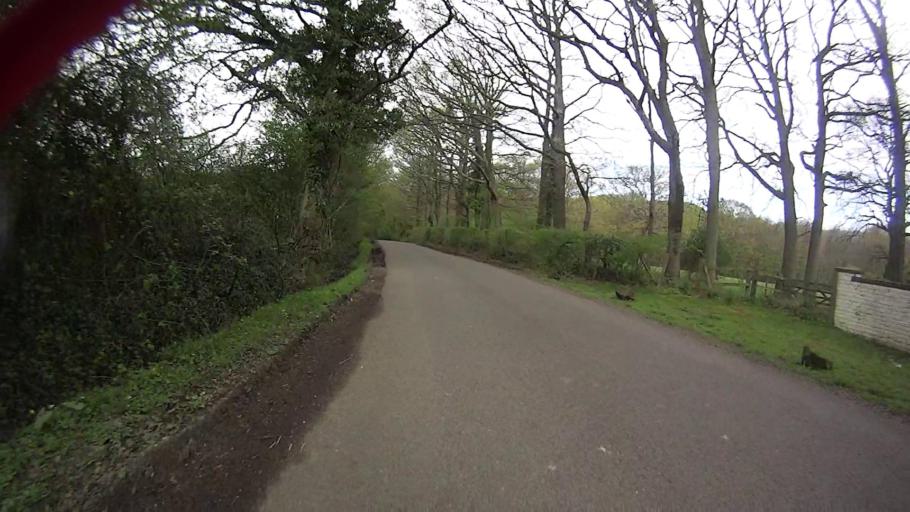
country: GB
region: England
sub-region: West Sussex
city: Bewbush
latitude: 51.1328
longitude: -0.2587
